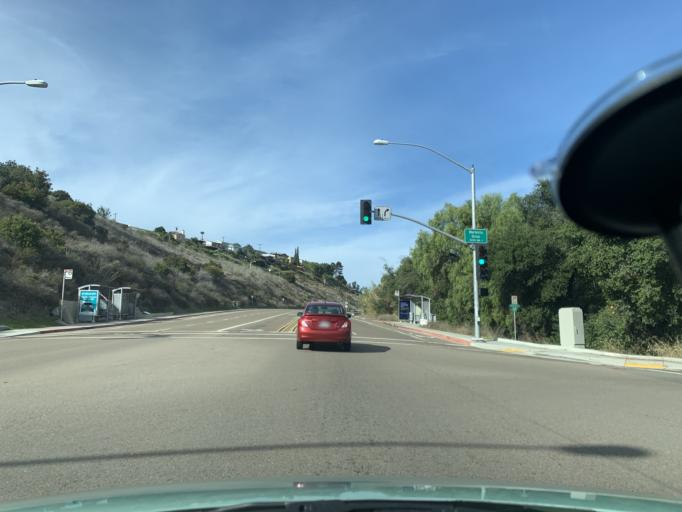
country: US
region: California
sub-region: San Diego County
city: San Diego
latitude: 32.8049
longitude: -117.1752
